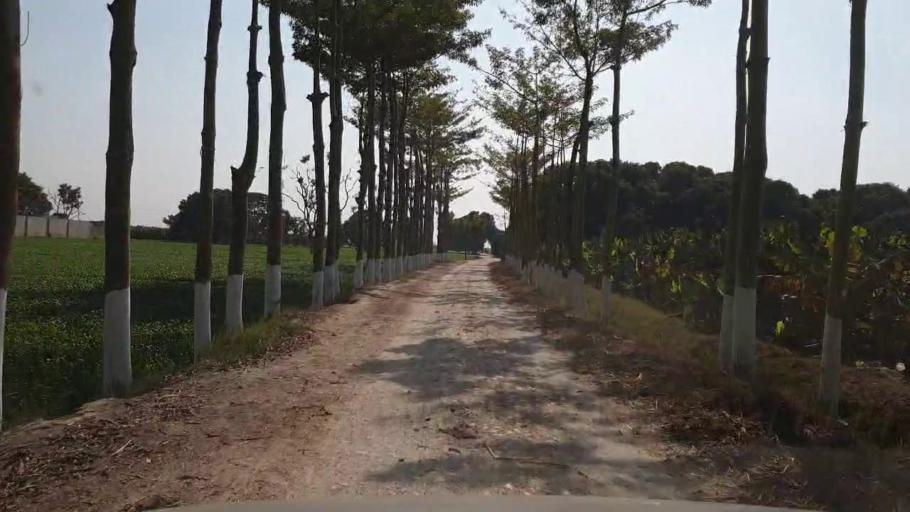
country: PK
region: Sindh
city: Tando Jam
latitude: 25.4027
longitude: 68.6280
